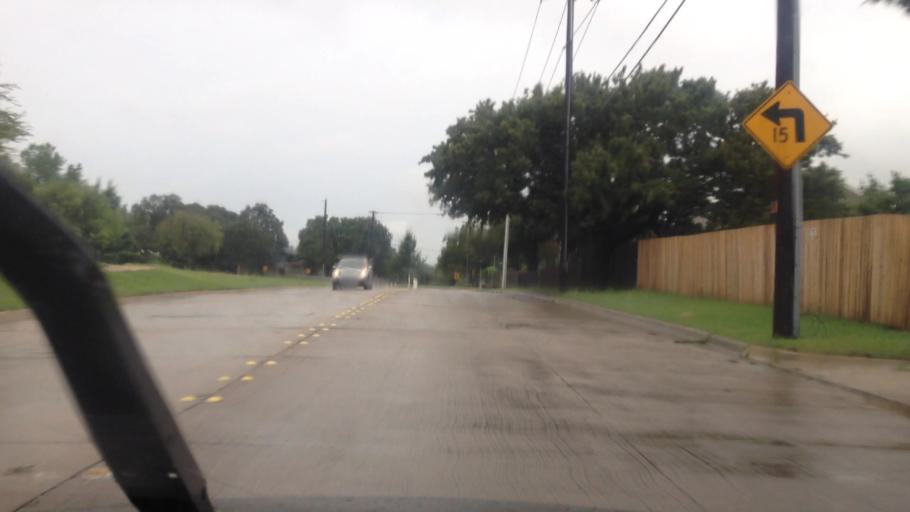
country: US
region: Texas
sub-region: Tarrant County
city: Watauga
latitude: 32.8872
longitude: -97.2292
